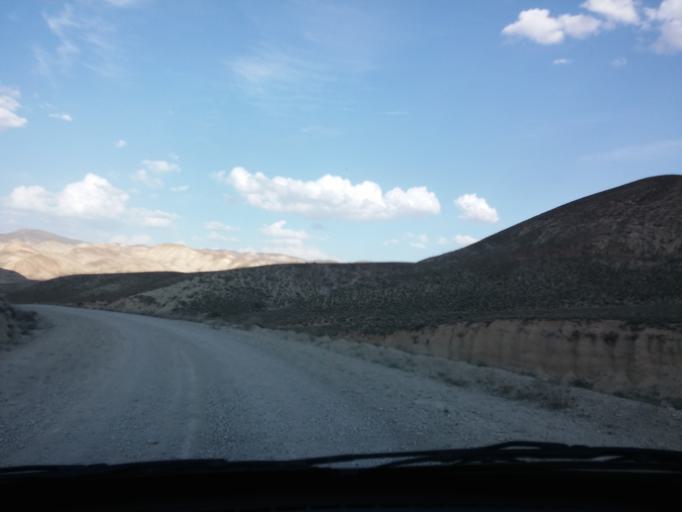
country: IR
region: Tehran
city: Damavand
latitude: 35.5325
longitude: 52.2268
